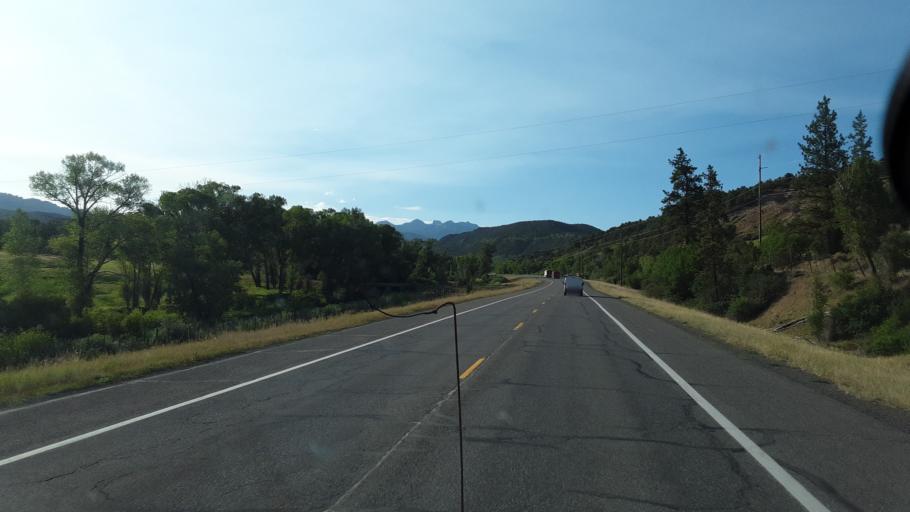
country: US
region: Colorado
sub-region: Ouray County
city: Ouray
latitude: 38.2373
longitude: -107.7380
